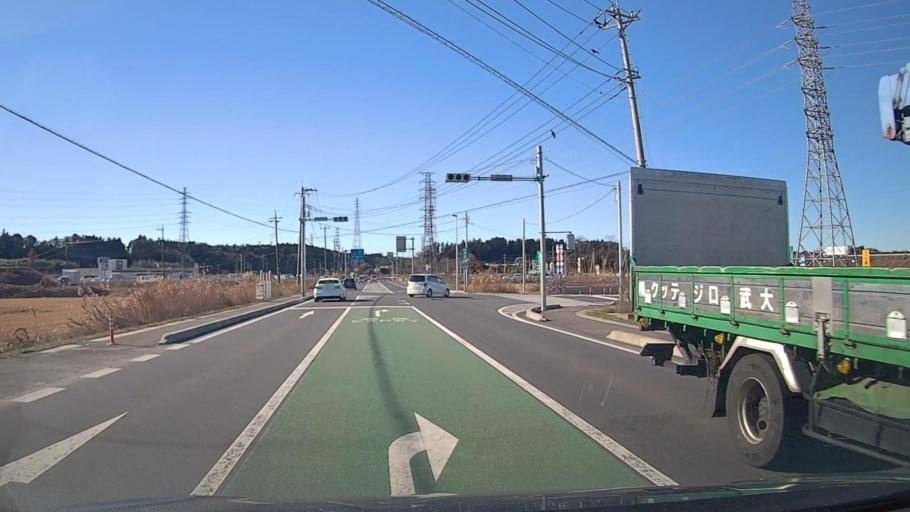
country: JP
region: Ibaraki
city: Mito-shi
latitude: 36.4152
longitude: 140.4273
